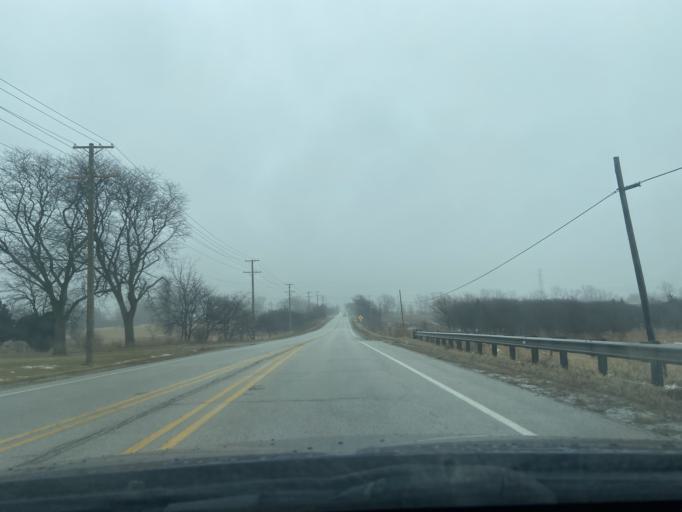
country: US
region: Illinois
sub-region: Lake County
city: Volo
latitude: 42.3177
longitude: -88.1248
